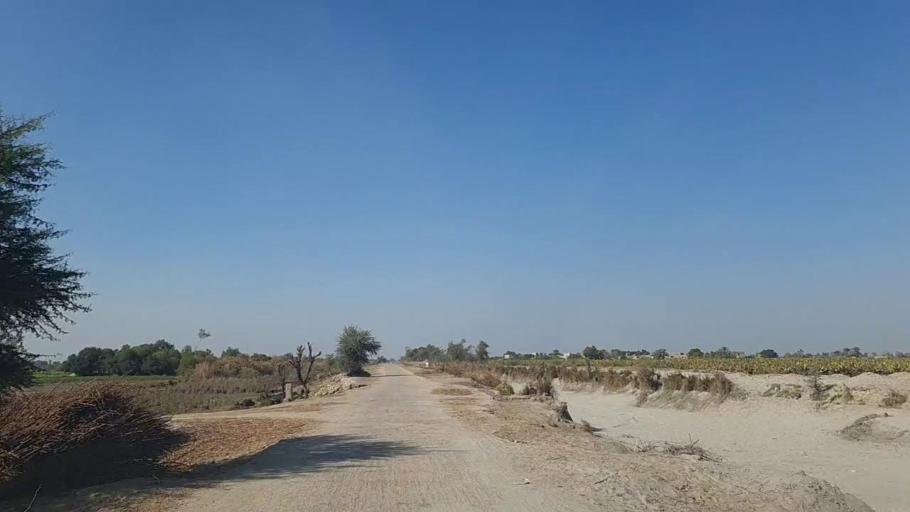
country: PK
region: Sindh
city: Shahpur Chakar
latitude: 26.2186
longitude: 68.6045
